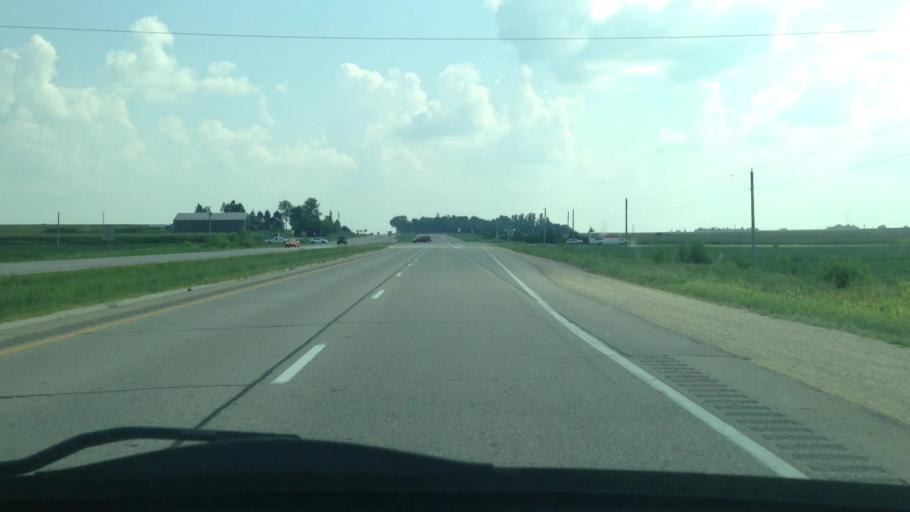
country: US
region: Iowa
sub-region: Bremer County
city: Denver
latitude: 42.6165
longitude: -92.3378
